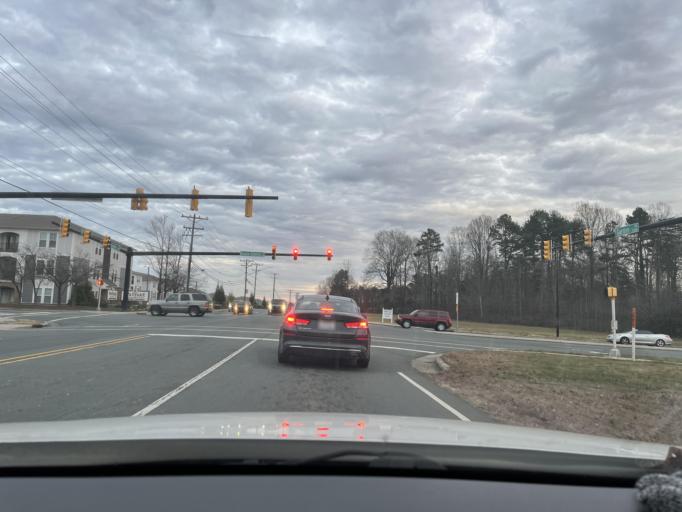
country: US
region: North Carolina
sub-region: Alamance County
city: Elon
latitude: 36.0716
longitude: -79.5040
